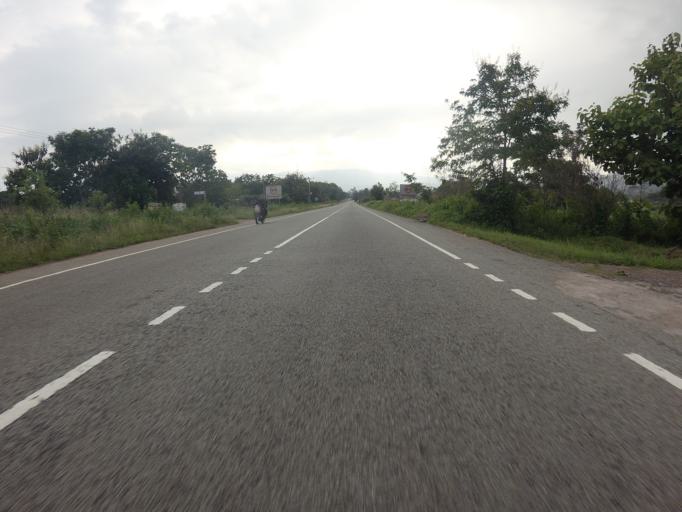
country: GH
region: Volta
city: Ho
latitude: 6.7843
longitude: 0.4471
